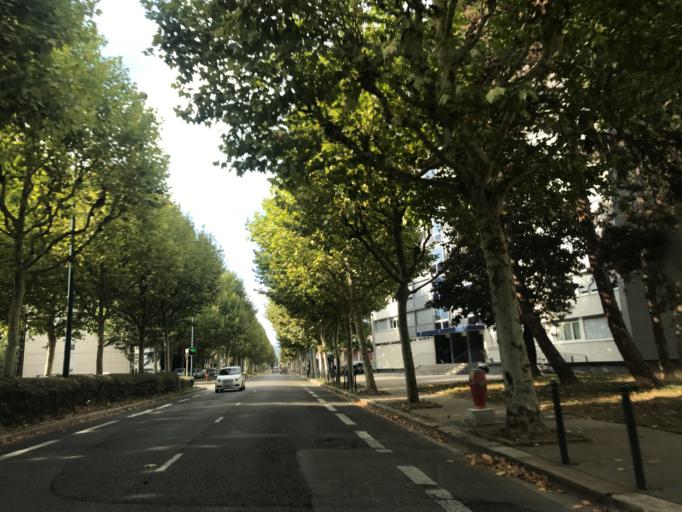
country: FR
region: Rhone-Alpes
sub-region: Departement de la Haute-Savoie
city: Annecy-le-Vieux
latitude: 45.9141
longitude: 6.1346
